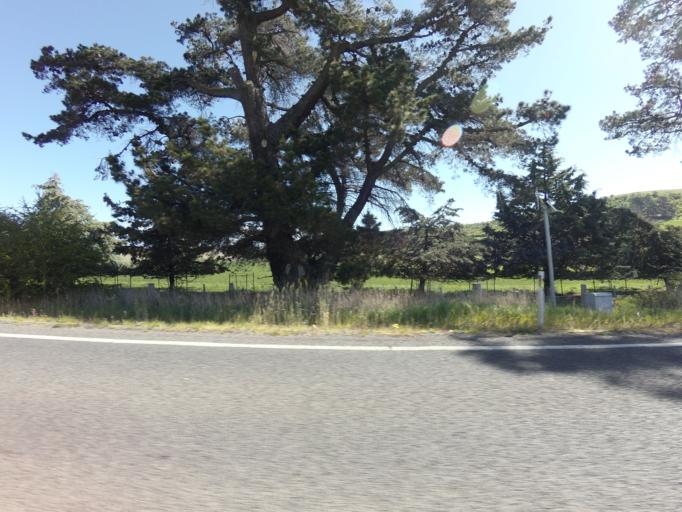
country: AU
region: Tasmania
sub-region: Derwent Valley
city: New Norfolk
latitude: -42.5654
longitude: 146.8803
